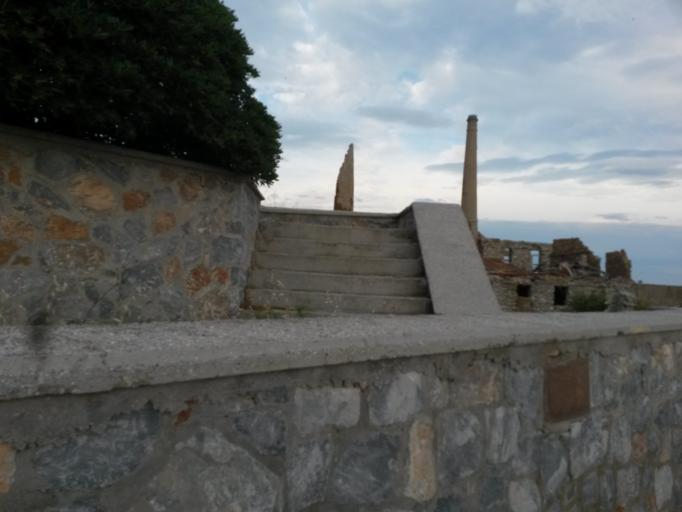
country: GR
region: North Aegean
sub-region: Nomos Lesvou
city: Plomarion
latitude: 38.9751
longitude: 26.3669
